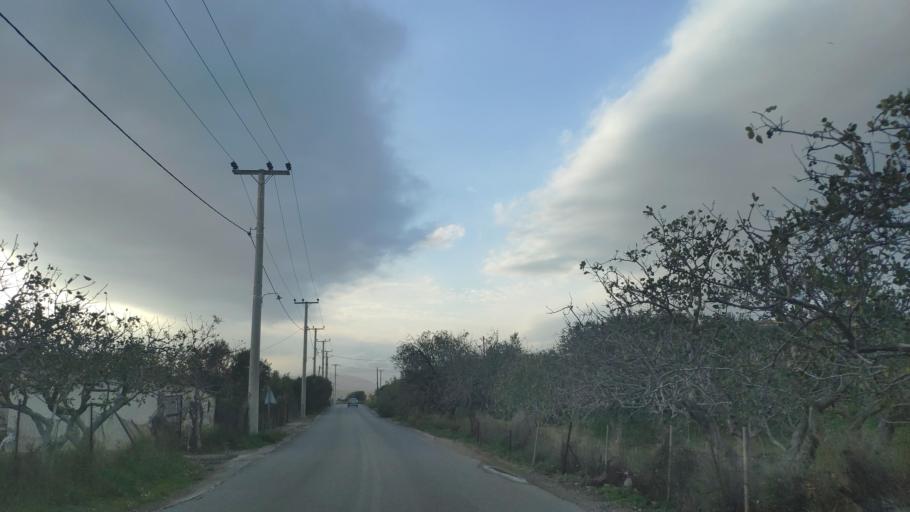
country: GR
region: Attica
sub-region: Nomarchia Dytikis Attikis
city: Nea Peramos
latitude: 37.9956
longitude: 23.3934
